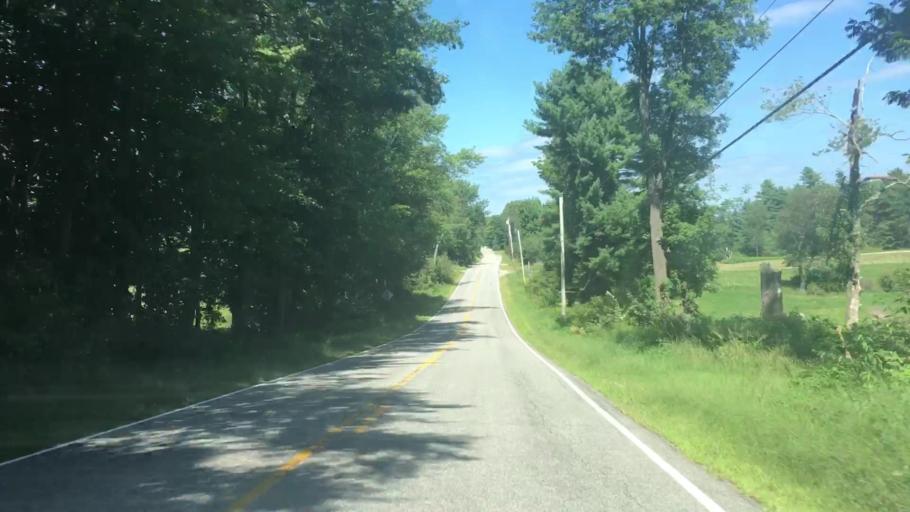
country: US
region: Maine
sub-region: Kennebec County
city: Monmouth
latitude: 44.1810
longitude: -69.9397
